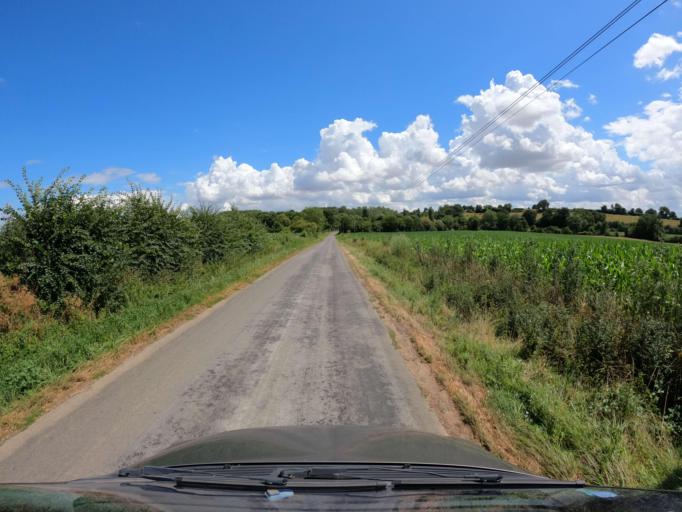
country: FR
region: Pays de la Loire
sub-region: Departement de la Sarthe
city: Brulon
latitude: 47.9484
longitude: -0.2442
